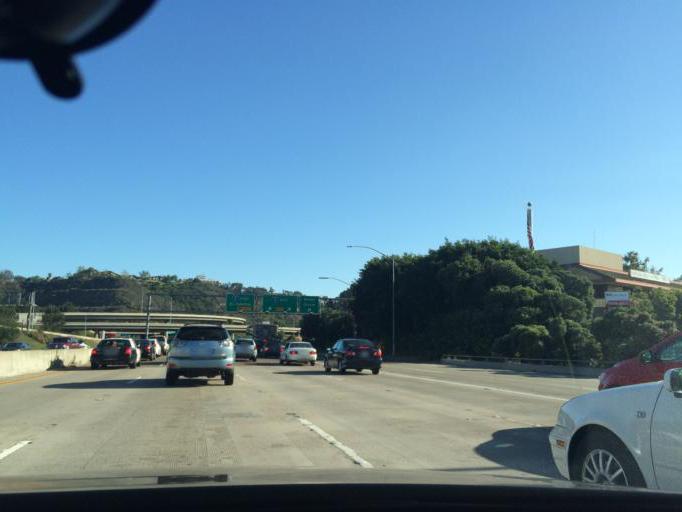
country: US
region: California
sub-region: San Diego County
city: San Diego
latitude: 32.7659
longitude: -117.1628
